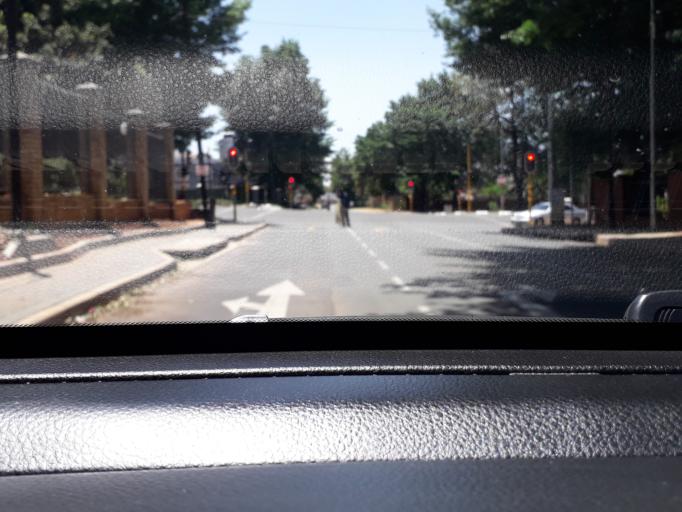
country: ZA
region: Gauteng
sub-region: City of Johannesburg Metropolitan Municipality
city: Modderfontein
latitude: -26.1002
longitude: 28.0639
